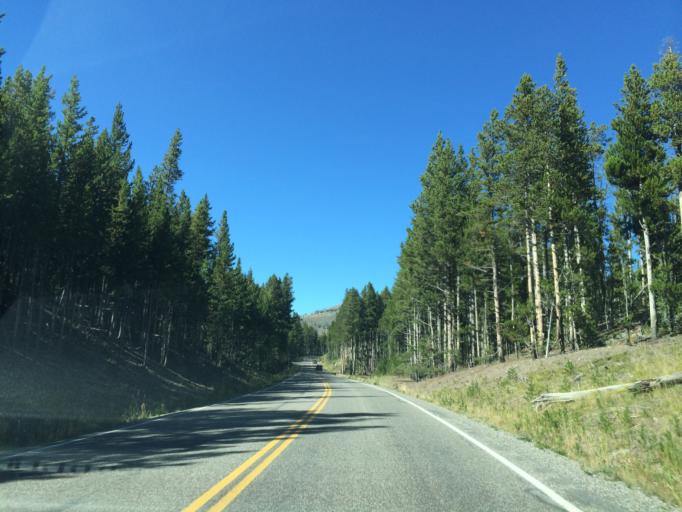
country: US
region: Montana
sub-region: Gallatin County
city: West Yellowstone
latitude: 44.7401
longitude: -110.4931
